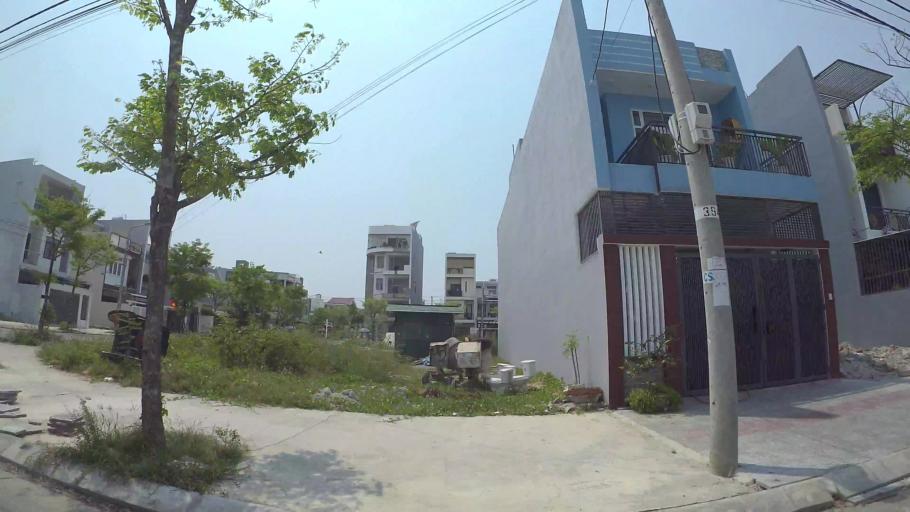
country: VN
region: Da Nang
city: Cam Le
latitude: 16.0109
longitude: 108.2214
